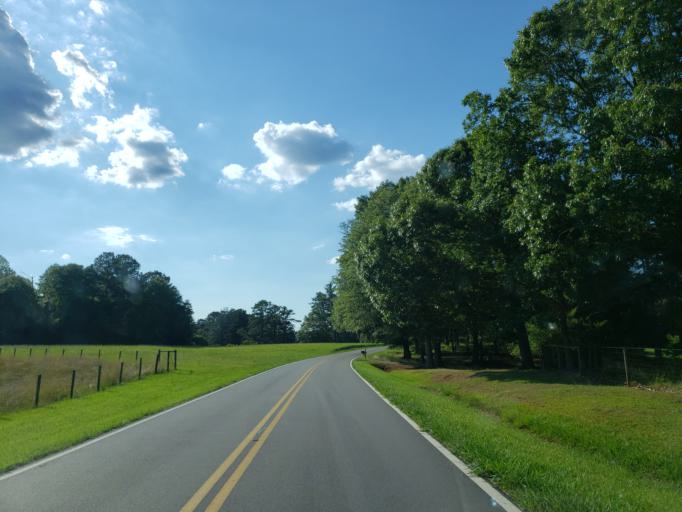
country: US
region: Georgia
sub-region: Haralson County
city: Bremen
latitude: 33.6667
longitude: -85.1148
